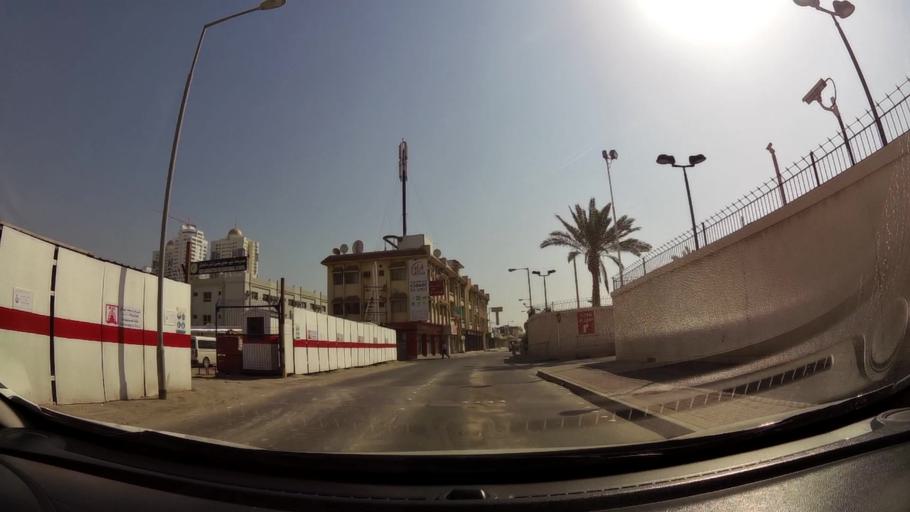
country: BH
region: Manama
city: Manama
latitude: 26.2098
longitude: 50.6029
